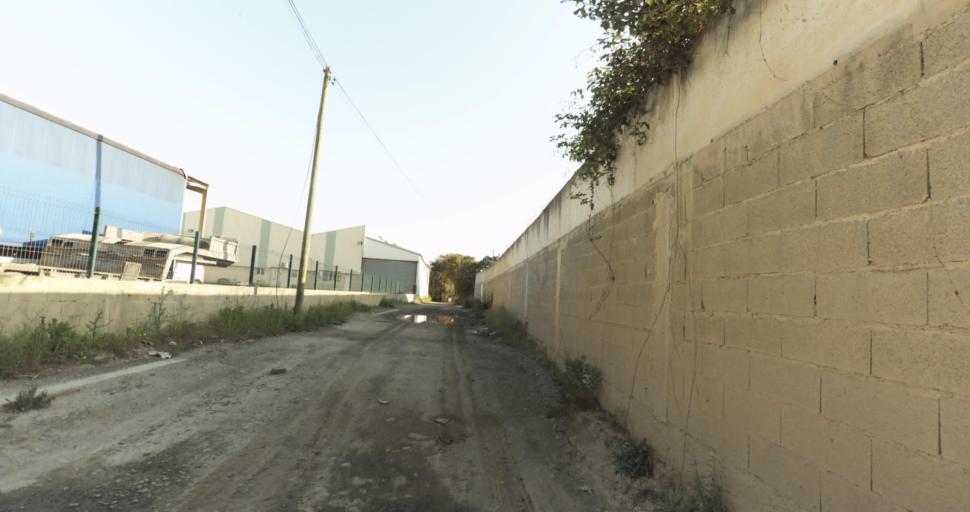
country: FR
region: Corsica
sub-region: Departement de la Haute-Corse
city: Biguglia
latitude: 42.6008
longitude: 9.4461
